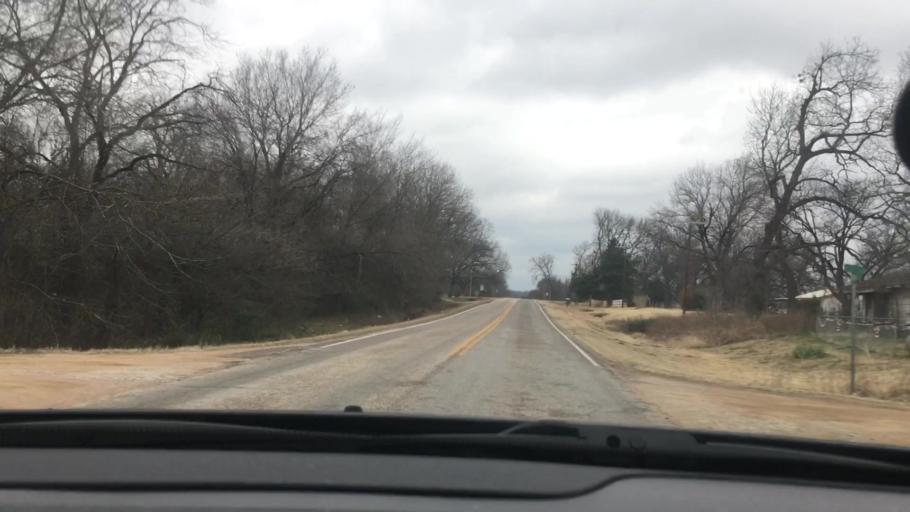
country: US
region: Oklahoma
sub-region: Coal County
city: Coalgate
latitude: 34.3750
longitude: -96.4304
